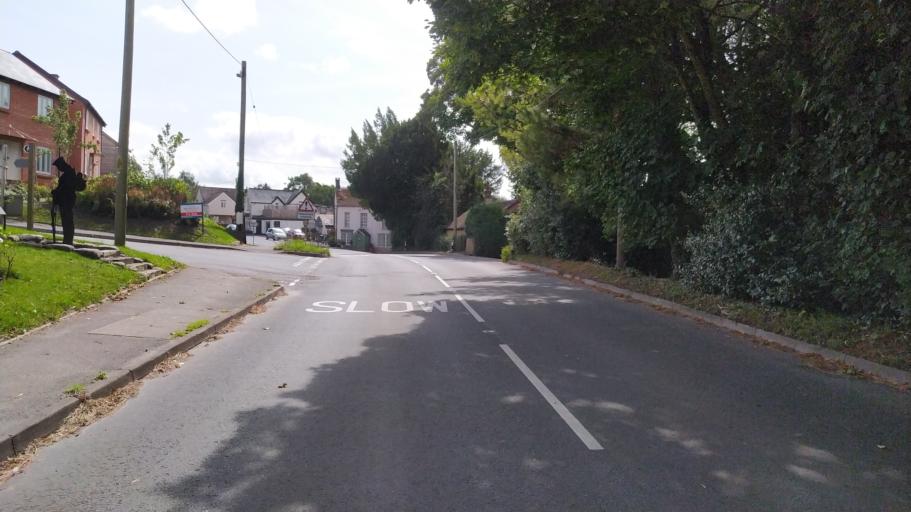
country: GB
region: England
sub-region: Dorset
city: Blandford Forum
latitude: 50.8854
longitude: -2.1976
